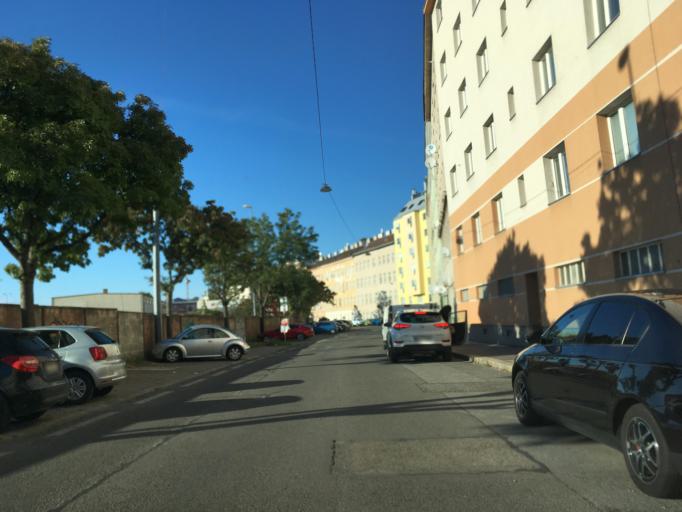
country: AT
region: Vienna
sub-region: Wien Stadt
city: Vienna
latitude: 48.2283
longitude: 16.3876
